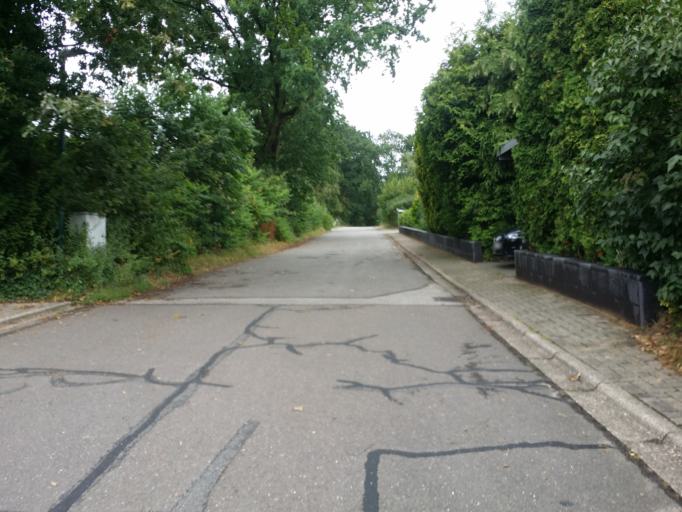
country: DE
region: Schleswig-Holstein
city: Oldendorf
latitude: 53.9467
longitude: 9.4597
